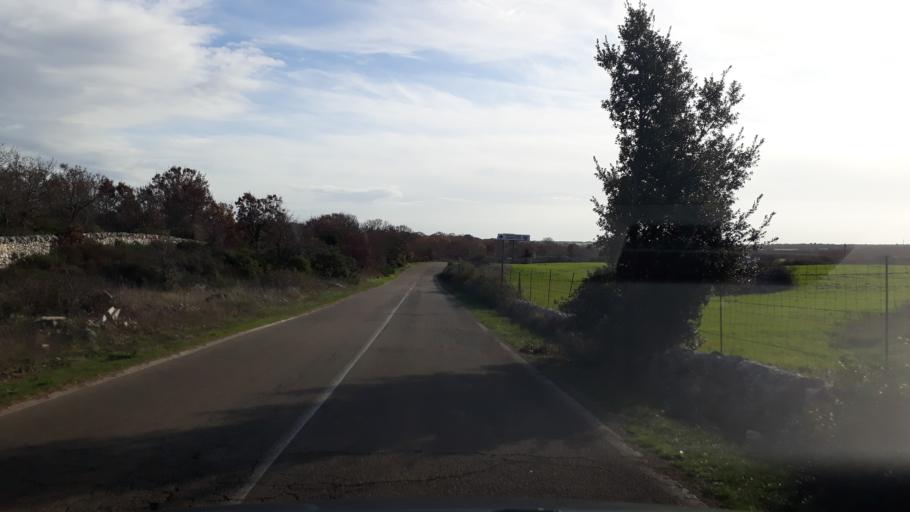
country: IT
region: Apulia
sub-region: Provincia di Taranto
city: Martina Franca
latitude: 40.6618
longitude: 17.3743
